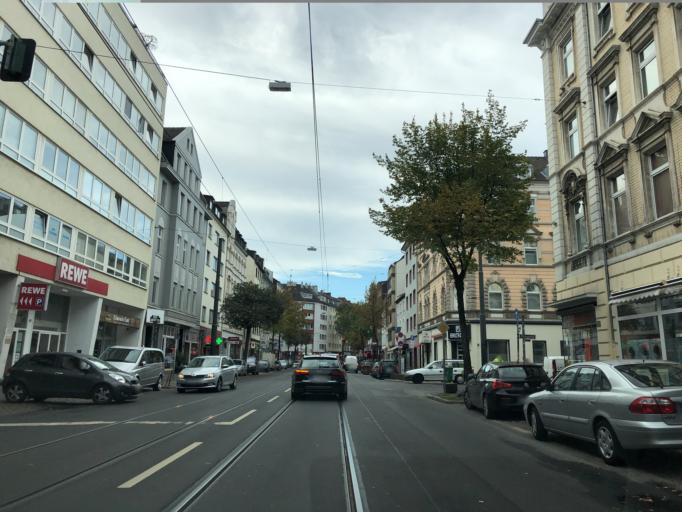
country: DE
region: North Rhine-Westphalia
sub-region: Regierungsbezirk Dusseldorf
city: Dusseldorf
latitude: 51.2109
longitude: 6.7689
